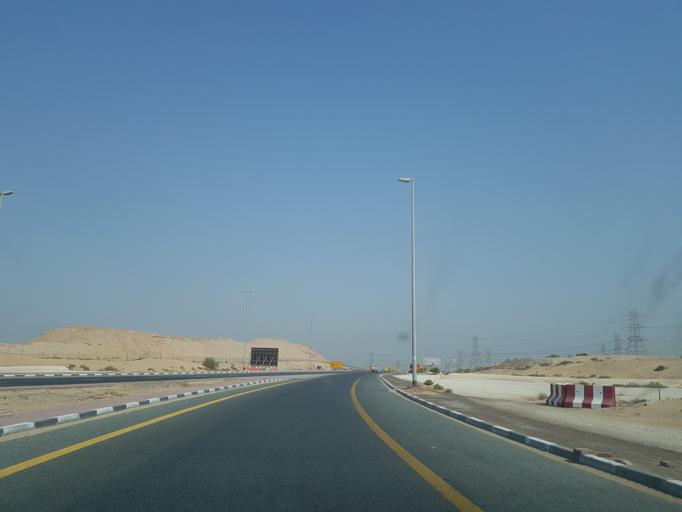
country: AE
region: Ash Shariqah
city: Sharjah
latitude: 25.1397
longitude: 55.4265
